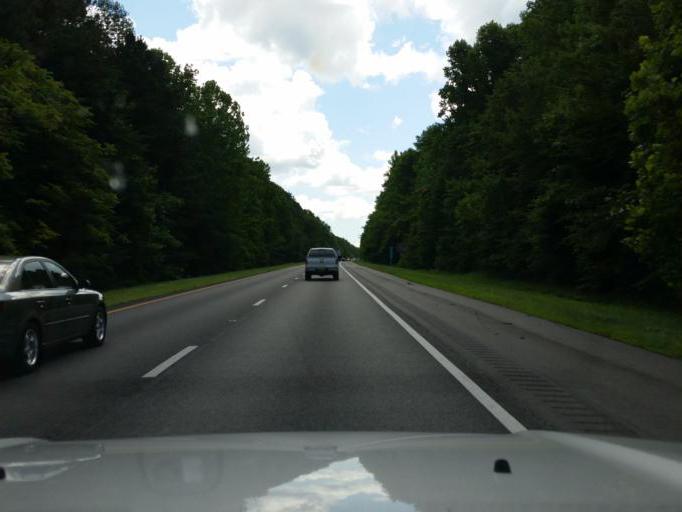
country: US
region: Virginia
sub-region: King William County
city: West Point
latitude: 37.4093
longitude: -76.7933
